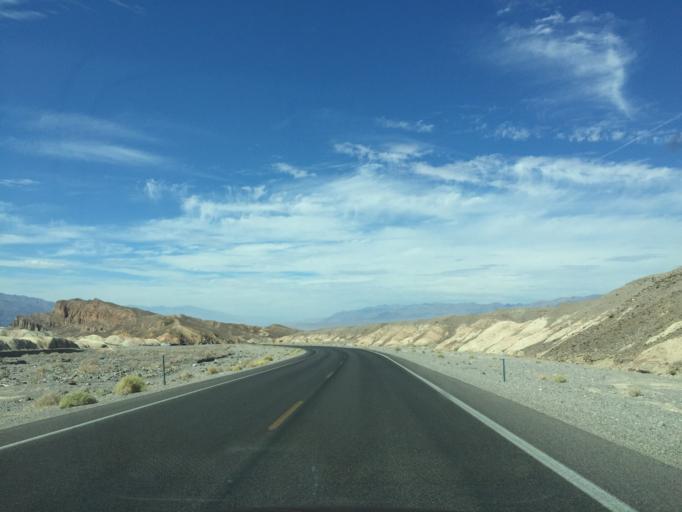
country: US
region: Nevada
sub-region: Nye County
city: Beatty
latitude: 36.4174
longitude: -116.8048
